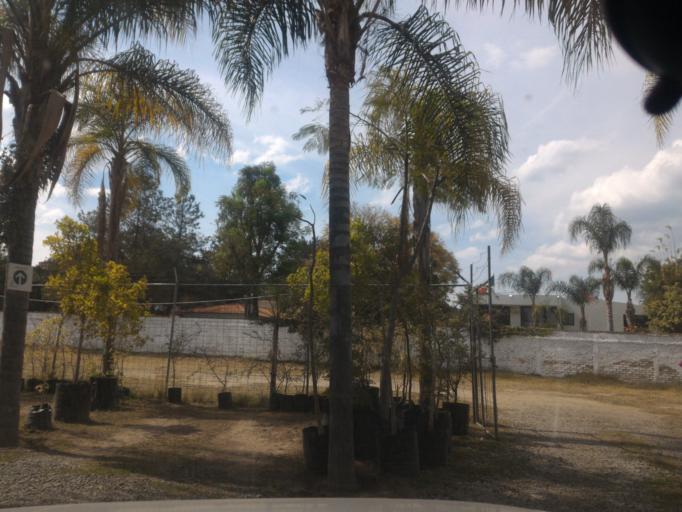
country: MX
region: Jalisco
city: Nicolas R Casillas
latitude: 20.5517
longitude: -103.4585
